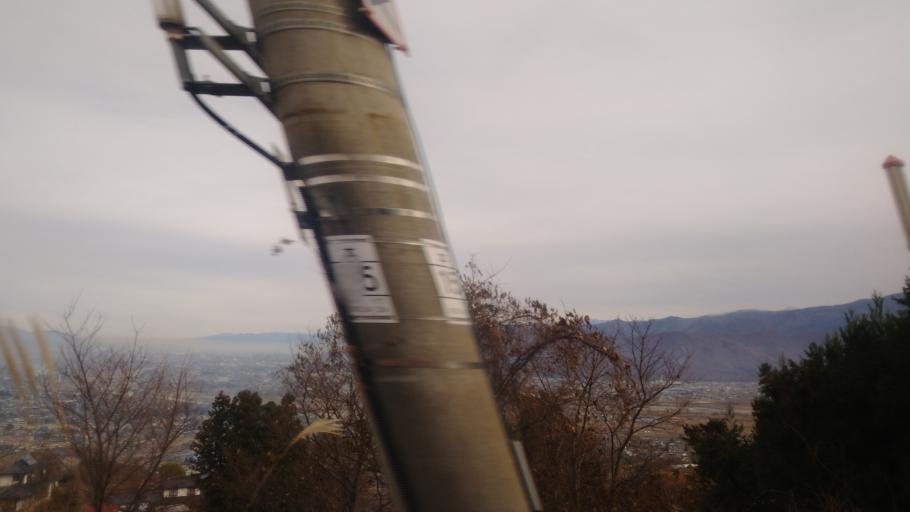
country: JP
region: Nagano
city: Nagano-shi
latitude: 36.5064
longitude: 138.0908
